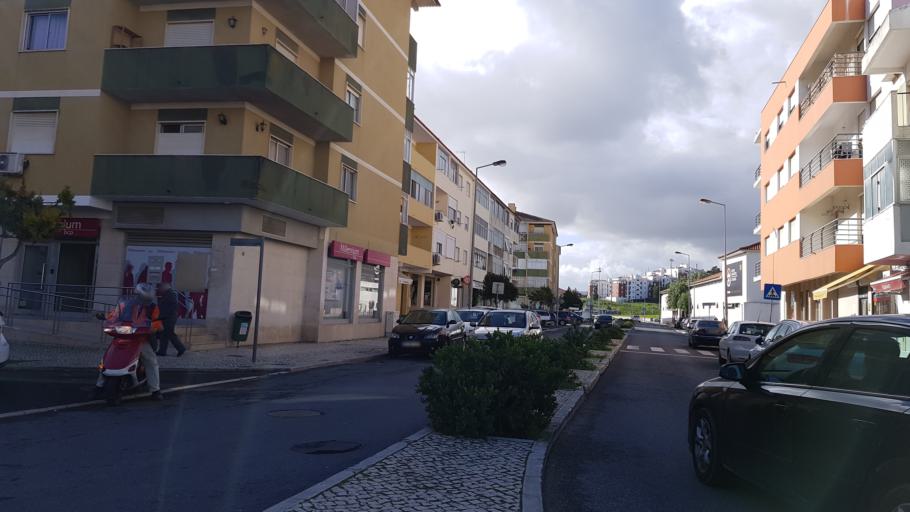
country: PT
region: Lisbon
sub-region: Azambuja
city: Azambuja
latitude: 39.0677
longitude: -8.8728
